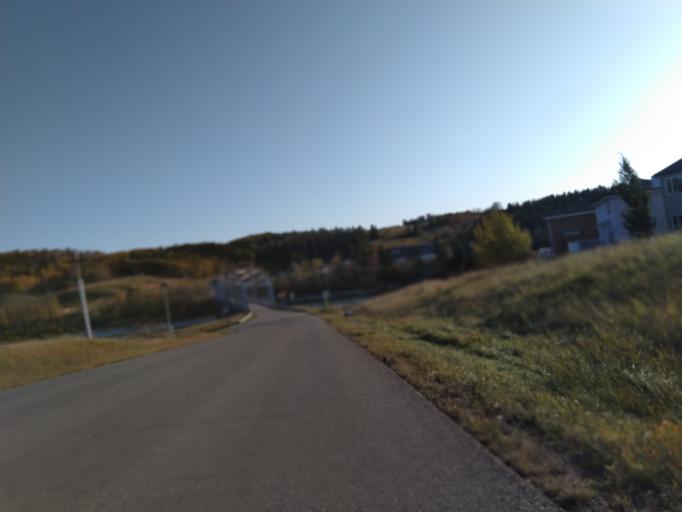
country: CA
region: Alberta
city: Cochrane
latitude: 51.1745
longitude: -114.4670
